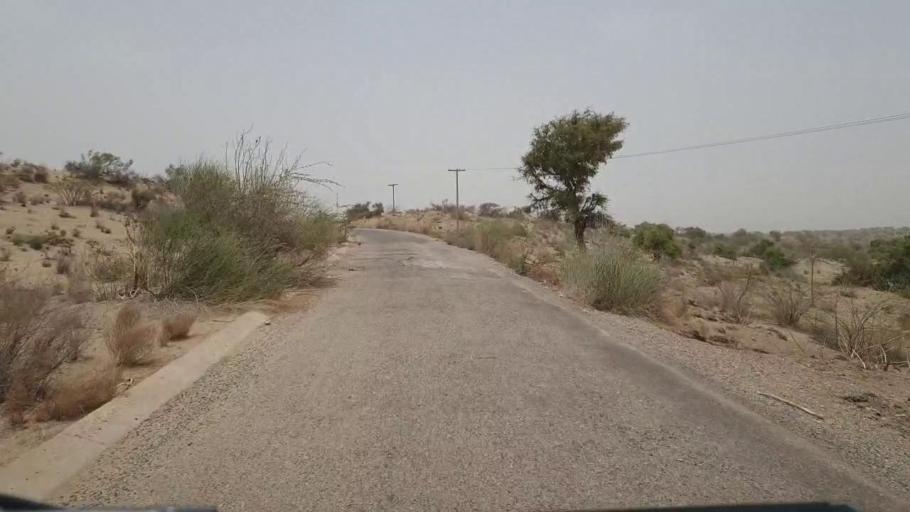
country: PK
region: Sindh
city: Naukot
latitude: 24.7549
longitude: 69.5525
